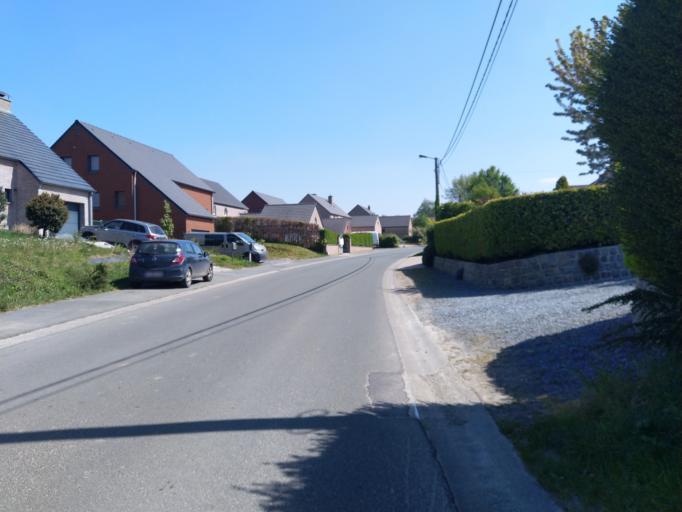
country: BE
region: Wallonia
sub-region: Province du Hainaut
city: Enghien
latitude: 50.6620
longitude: 4.0555
